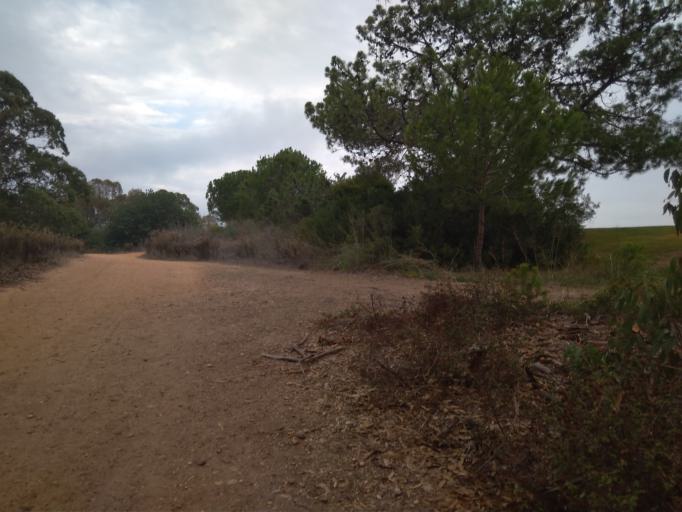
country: PT
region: Faro
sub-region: Loule
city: Almancil
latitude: 37.0261
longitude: -8.0057
